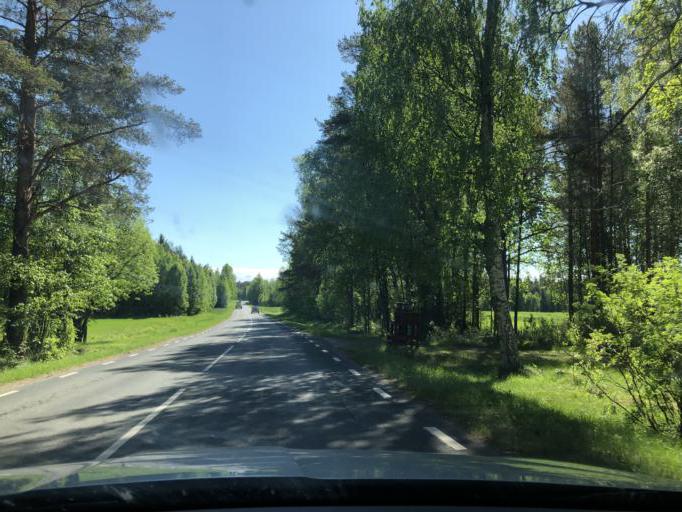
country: SE
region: Norrbotten
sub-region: Lulea Kommun
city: Gammelstad
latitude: 65.6611
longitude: 21.9801
